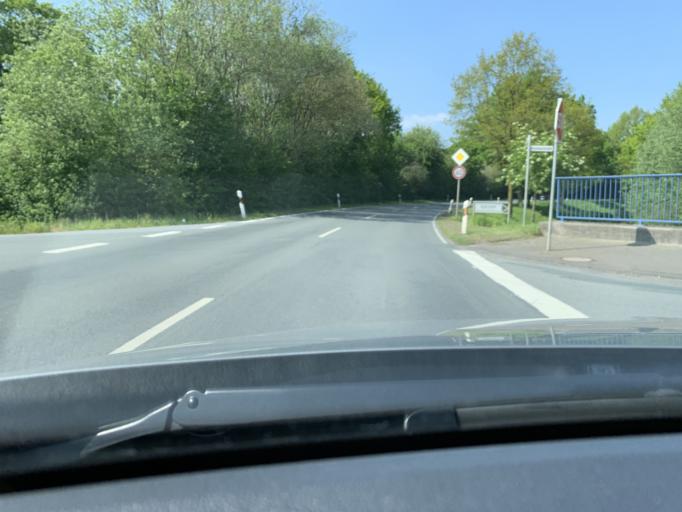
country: DE
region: North Rhine-Westphalia
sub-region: Regierungsbezirk Detmold
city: Langenberg
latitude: 51.7983
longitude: 8.3677
